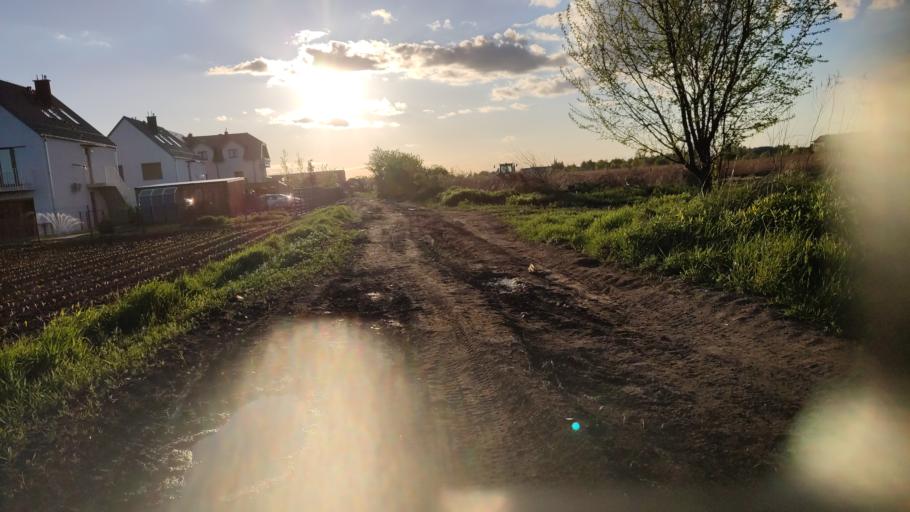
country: PL
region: Lower Silesian Voivodeship
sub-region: Powiat wroclawski
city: Zerniki Wroclawskie
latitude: 51.0479
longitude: 17.0417
